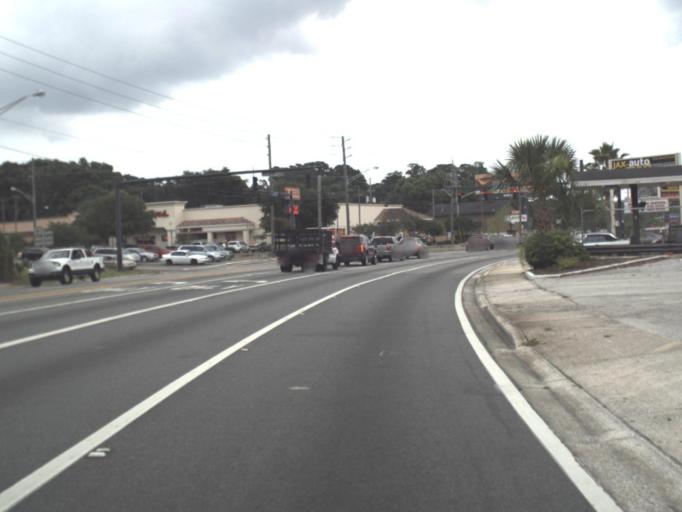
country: US
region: Florida
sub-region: Duval County
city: Jacksonville
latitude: 30.3139
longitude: -81.6004
